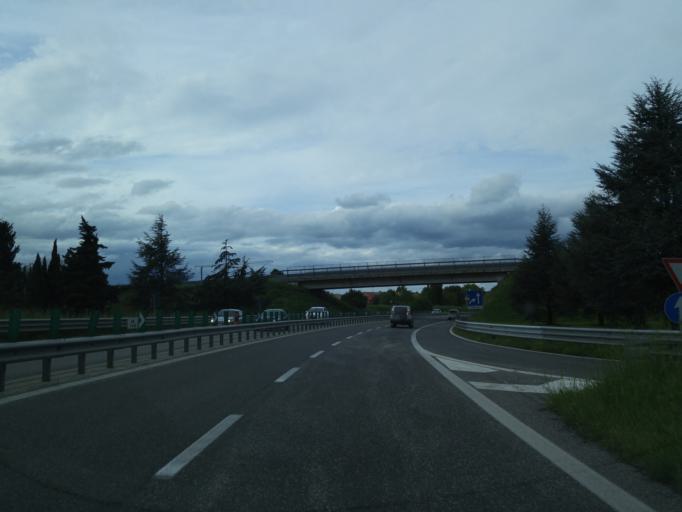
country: IT
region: The Marches
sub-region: Provincia di Pesaro e Urbino
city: Rosciano
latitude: 43.8218
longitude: 13.0147
